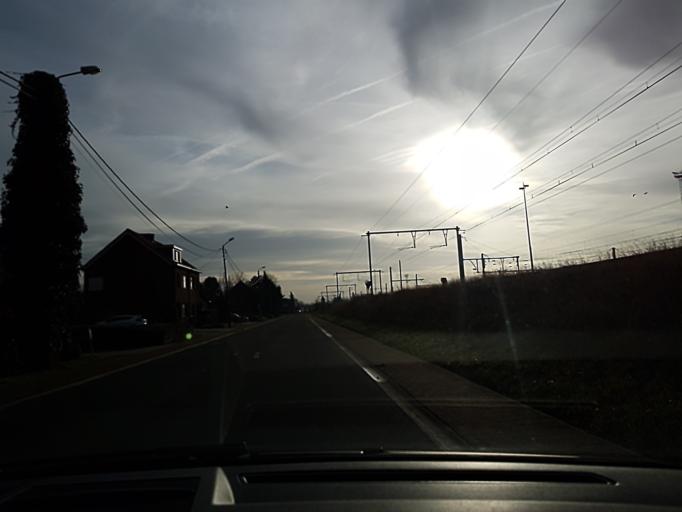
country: BE
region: Flanders
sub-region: Provincie Antwerpen
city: Mechelen
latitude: 51.0140
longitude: 4.5071
